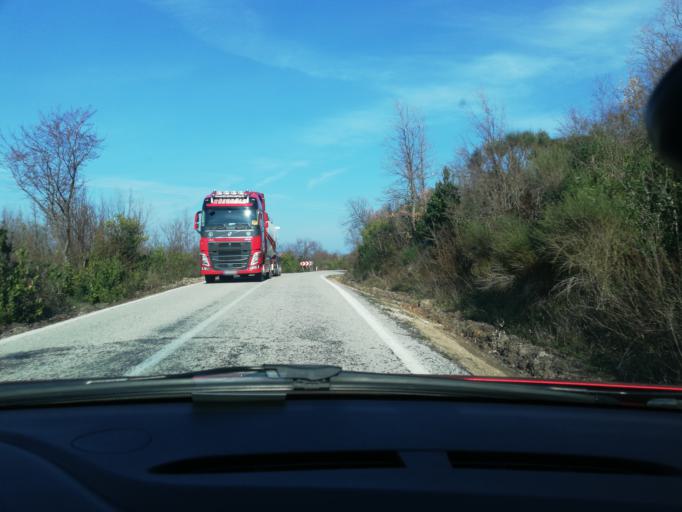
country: TR
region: Bartin
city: Kurucasile
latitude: 41.8580
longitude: 32.7810
